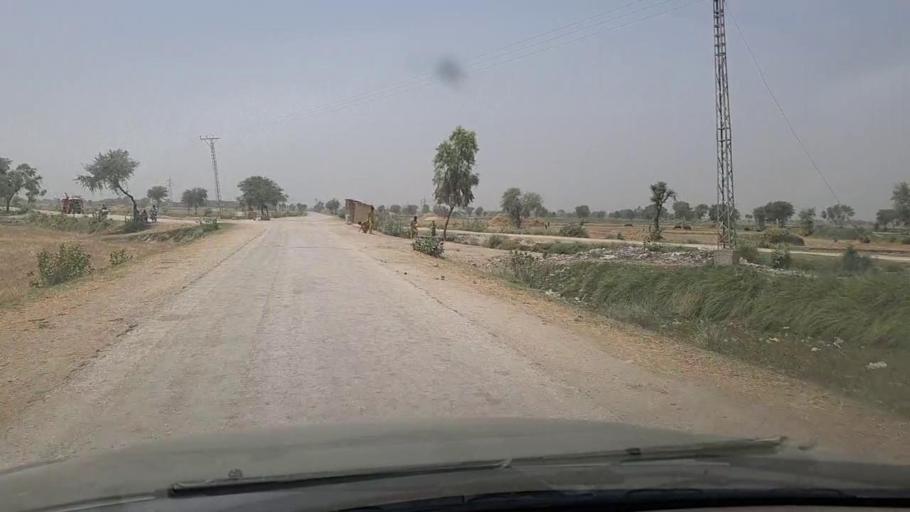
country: PK
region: Sindh
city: Ratodero
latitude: 27.7987
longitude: 68.2665
